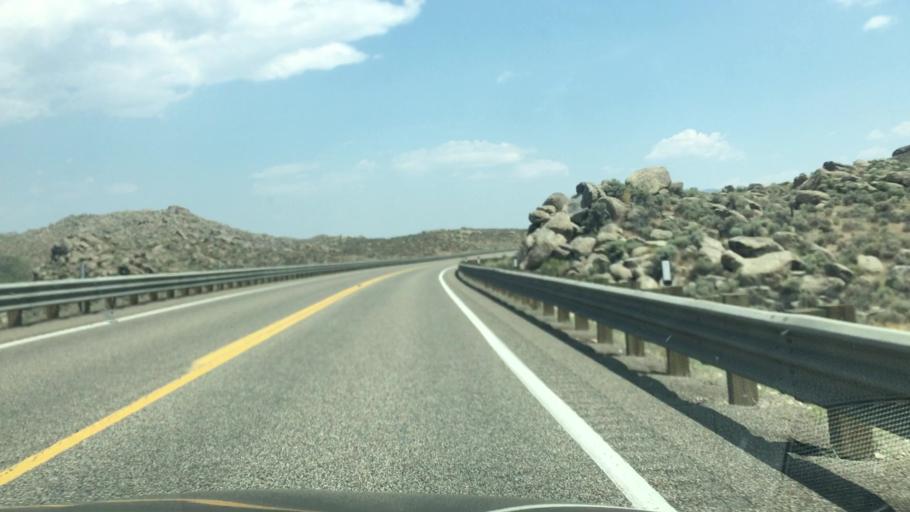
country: US
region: Nevada
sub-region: Elko County
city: Jackpot
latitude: 41.7356
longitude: -114.7876
